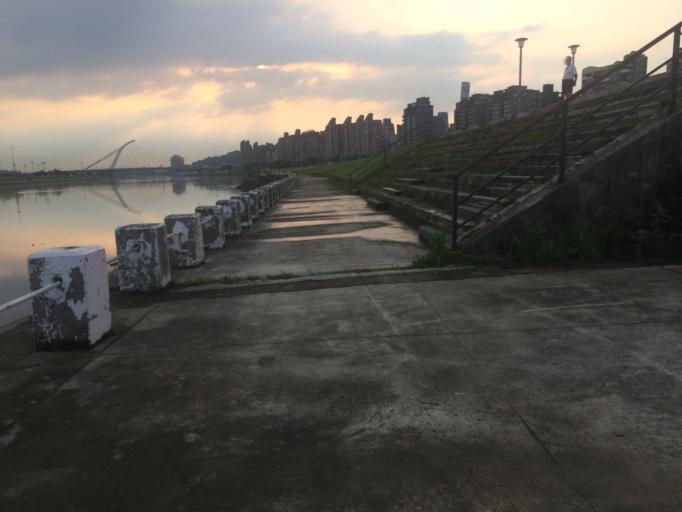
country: TW
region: Taipei
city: Taipei
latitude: 25.0755
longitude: 121.5570
